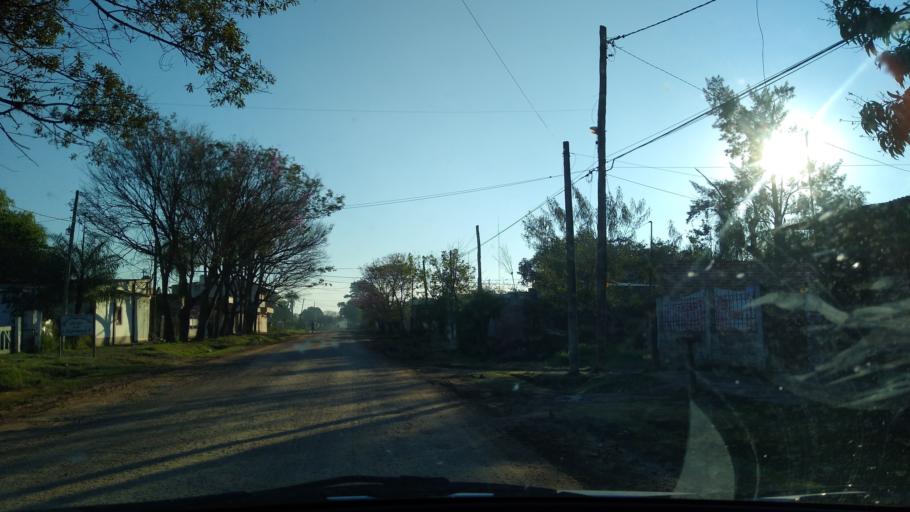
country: AR
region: Chaco
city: Resistencia
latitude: -27.4855
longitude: -58.9736
